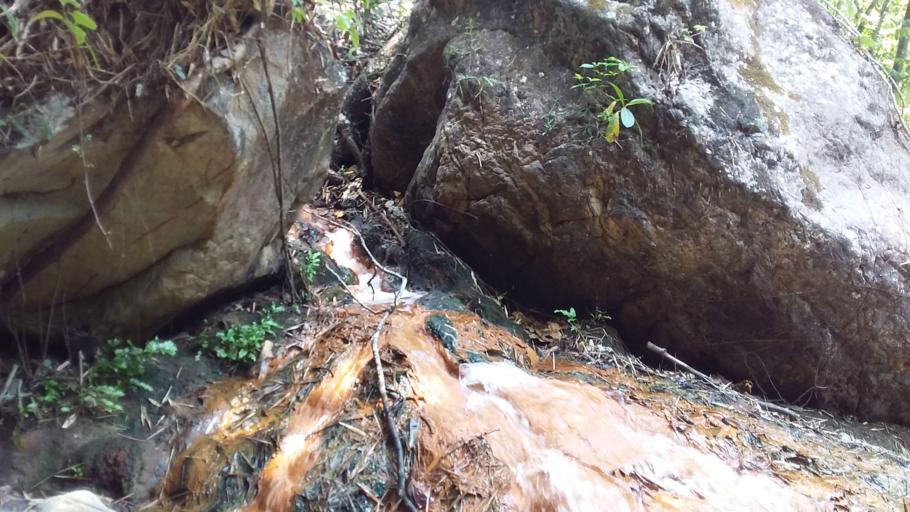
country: CO
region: Casanare
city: Nunchia
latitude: 5.6098
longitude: -72.2943
